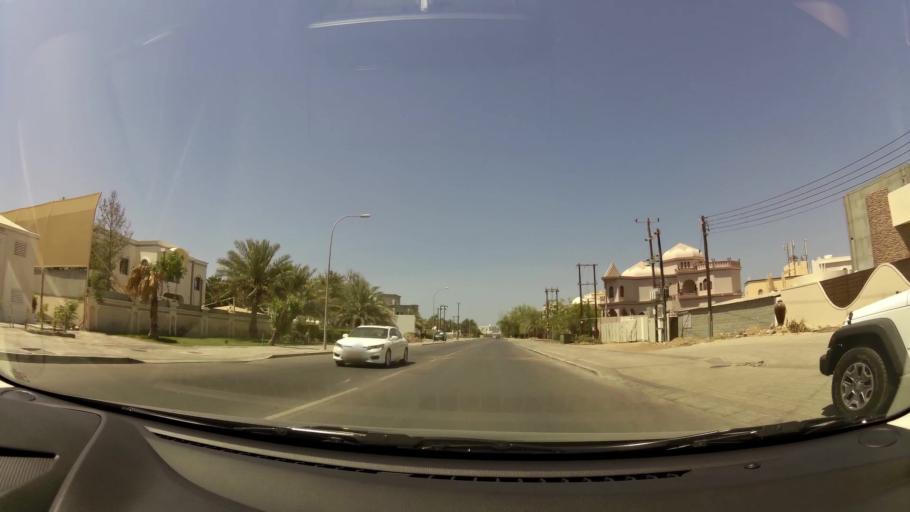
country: OM
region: Muhafazat Masqat
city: As Sib al Jadidah
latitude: 23.6276
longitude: 58.2232
